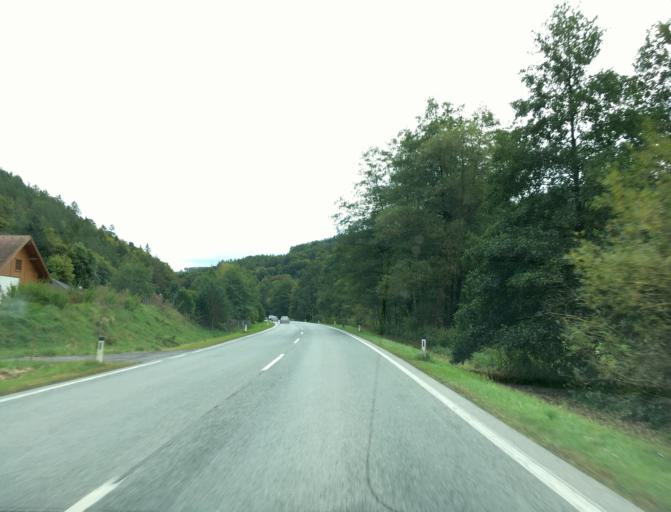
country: AT
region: Lower Austria
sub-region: Politischer Bezirk Wiener Neustadt
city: Bad Schonau
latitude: 47.5021
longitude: 16.2080
